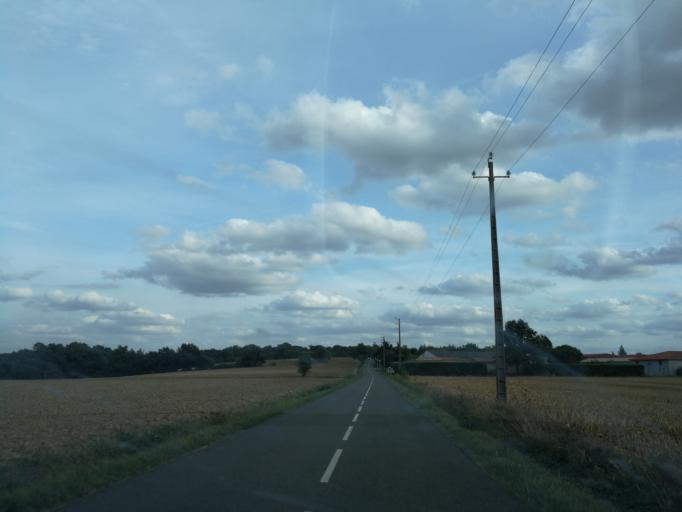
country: FR
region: Midi-Pyrenees
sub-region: Departement de la Haute-Garonne
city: Flourens
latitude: 43.6064
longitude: 1.5427
